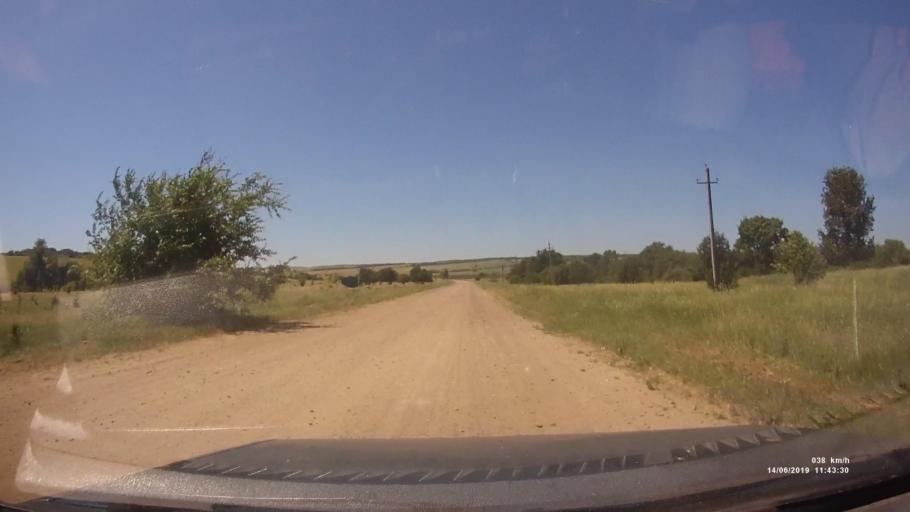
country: RU
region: Rostov
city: Kazanskaya
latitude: 49.8562
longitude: 41.3317
